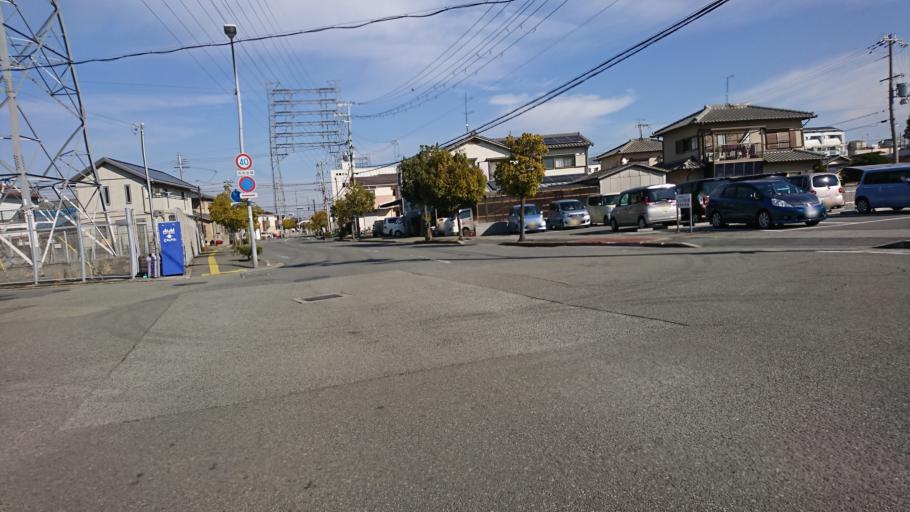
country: JP
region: Hyogo
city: Kakogawacho-honmachi
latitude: 34.7534
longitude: 134.7985
